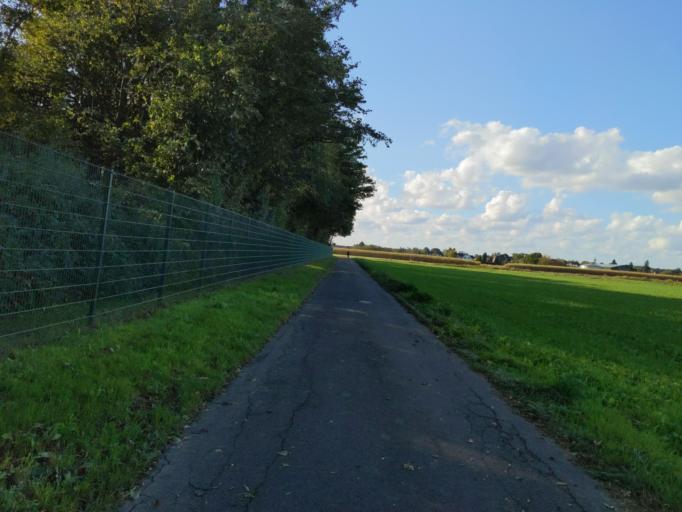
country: DE
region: North Rhine-Westphalia
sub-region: Regierungsbezirk Dusseldorf
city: Kaarst
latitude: 51.2119
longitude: 6.5991
